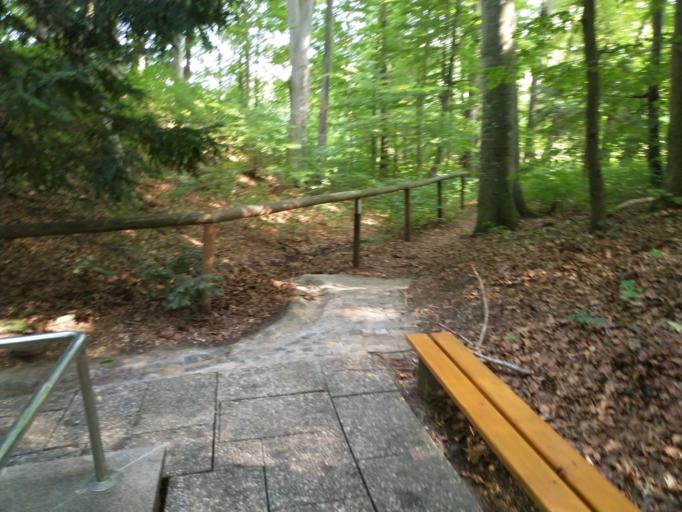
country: DE
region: Bavaria
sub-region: Swabia
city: Bad Worishofen
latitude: 48.0006
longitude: 10.5721
